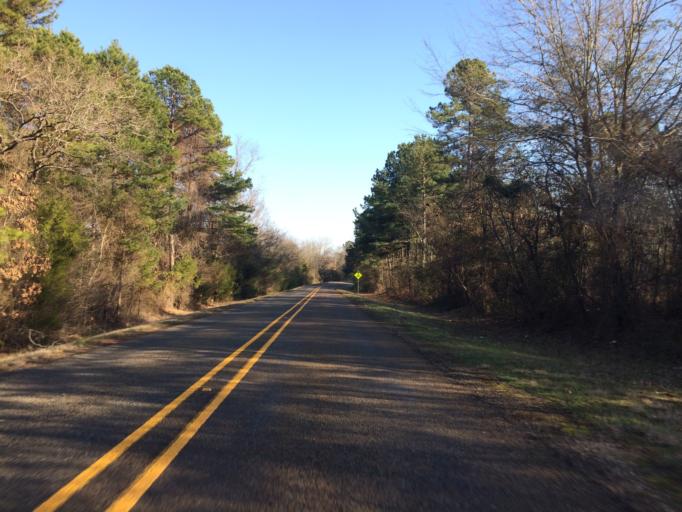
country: US
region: Texas
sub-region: Wood County
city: Hawkins
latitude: 32.6650
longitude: -95.3166
